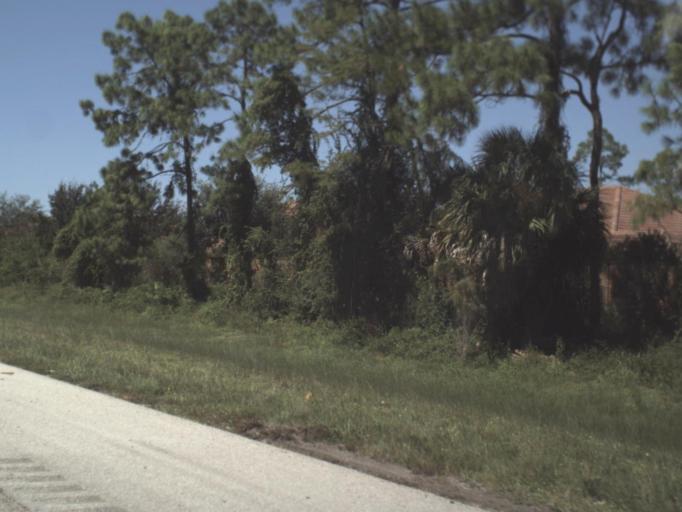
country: US
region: Florida
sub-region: Collier County
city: Golden Gate
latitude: 26.1647
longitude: -81.7056
